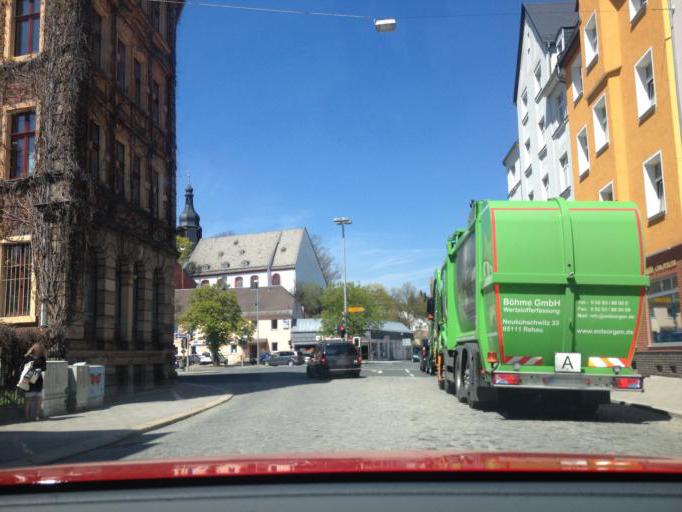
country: DE
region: Bavaria
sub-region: Upper Franconia
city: Hof
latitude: 50.3137
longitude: 11.9193
